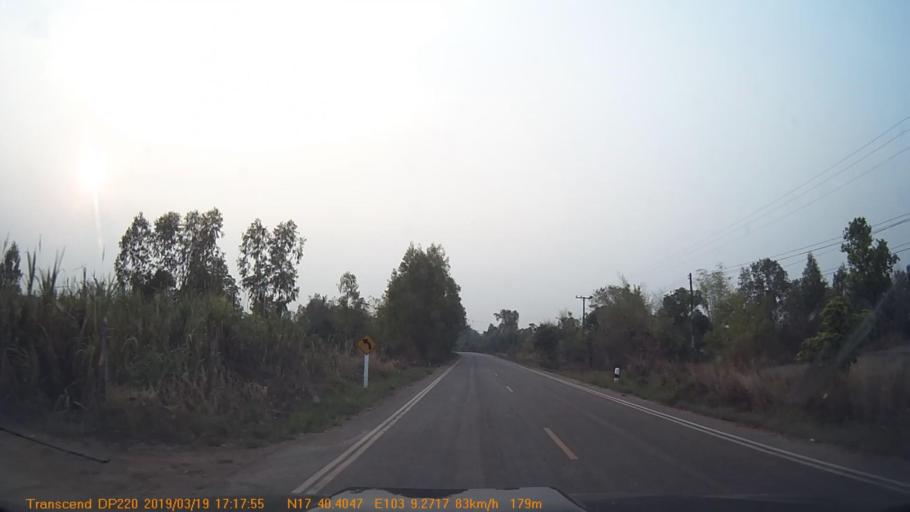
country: TH
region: Changwat Udon Thani
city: Ban Dung
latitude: 17.6738
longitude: 103.1540
